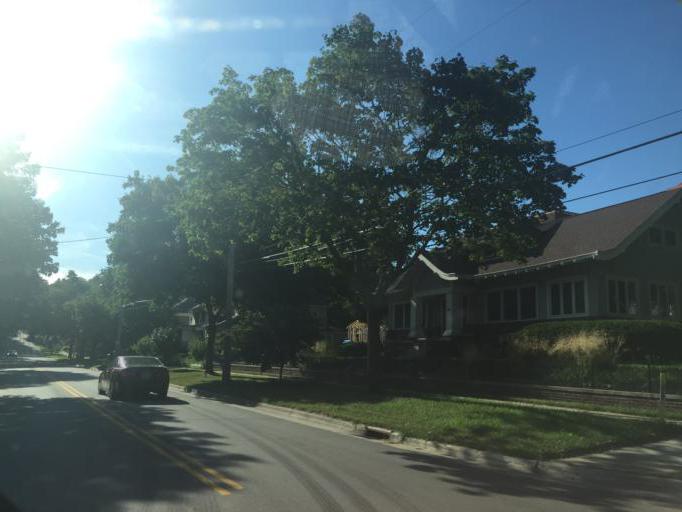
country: US
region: Minnesota
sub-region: Olmsted County
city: Rochester
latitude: 44.0171
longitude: -92.4731
